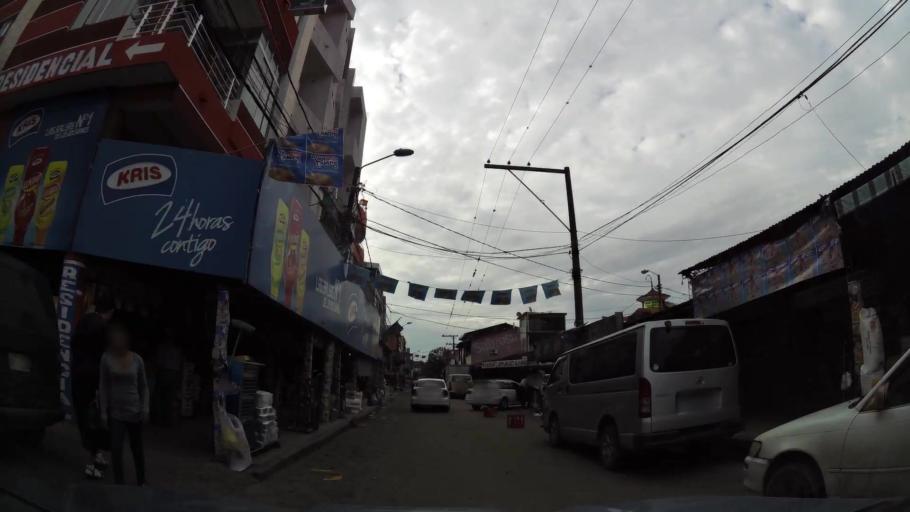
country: BO
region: Santa Cruz
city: Santa Cruz de la Sierra
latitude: -17.7771
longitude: -63.1764
